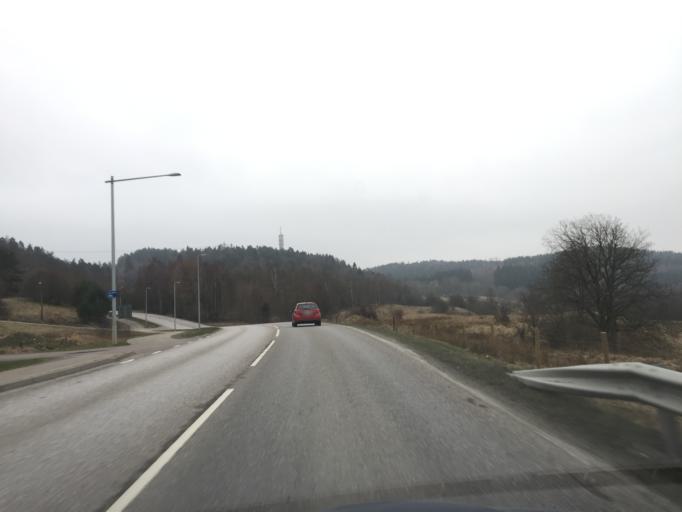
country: SE
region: Vaestra Goetaland
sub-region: Goteborg
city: Rannebergen
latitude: 57.7763
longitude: 12.0731
